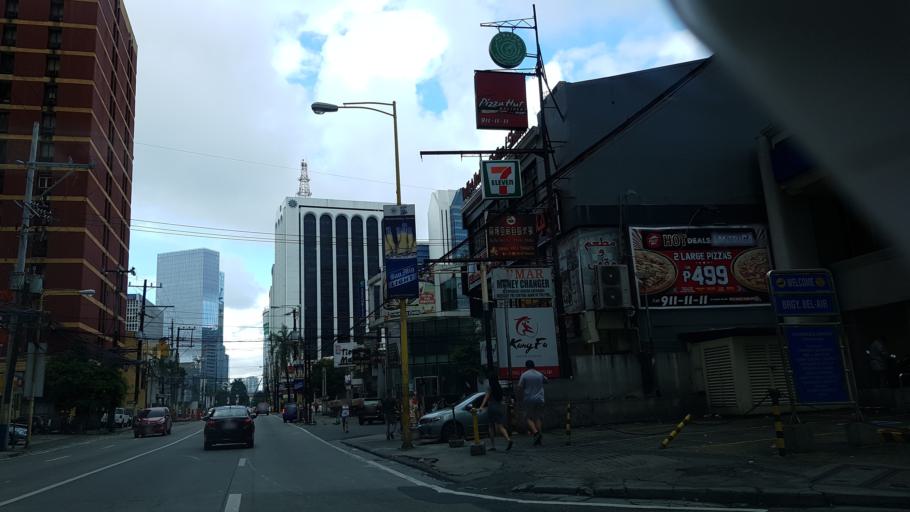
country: PH
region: Metro Manila
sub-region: Makati City
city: Makati City
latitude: 14.5643
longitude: 121.0292
